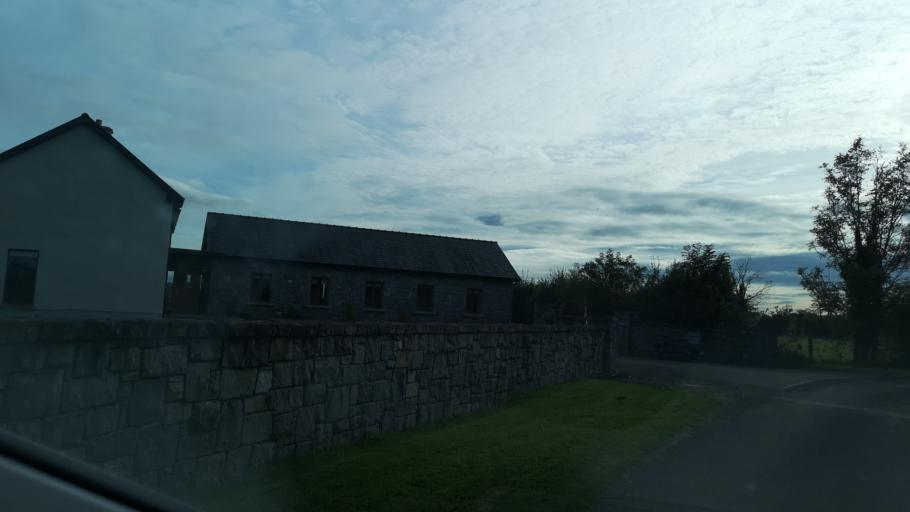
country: IE
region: Connaught
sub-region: County Galway
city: Ballinasloe
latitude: 53.3416
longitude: -8.2514
